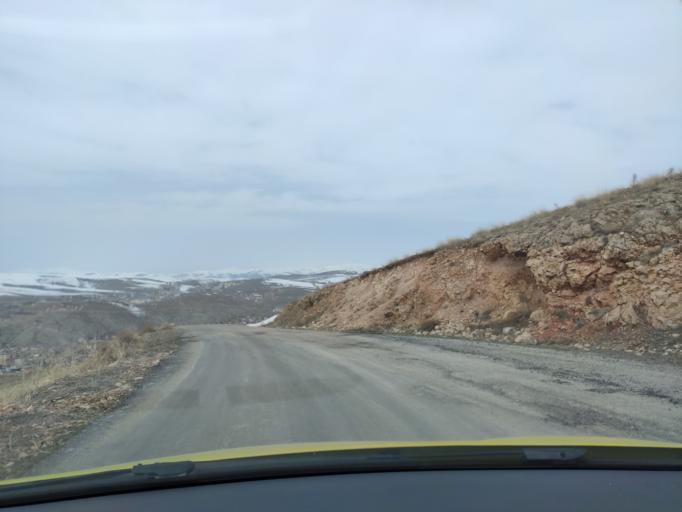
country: TR
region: Bayburt
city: Bayburt
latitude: 40.2576
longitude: 40.2411
